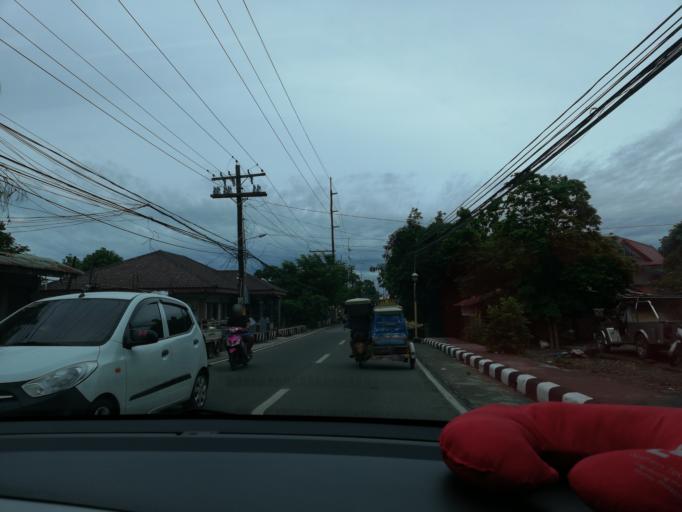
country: PH
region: Ilocos
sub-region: Province of Ilocos Sur
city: Vigan
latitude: 17.5767
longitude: 120.3855
